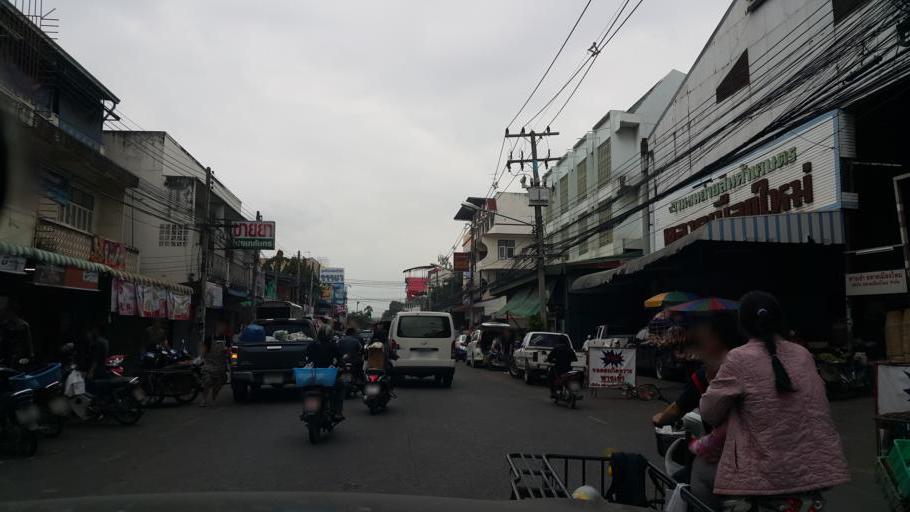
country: TH
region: Chiang Mai
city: Chiang Mai
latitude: 18.7979
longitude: 98.9974
